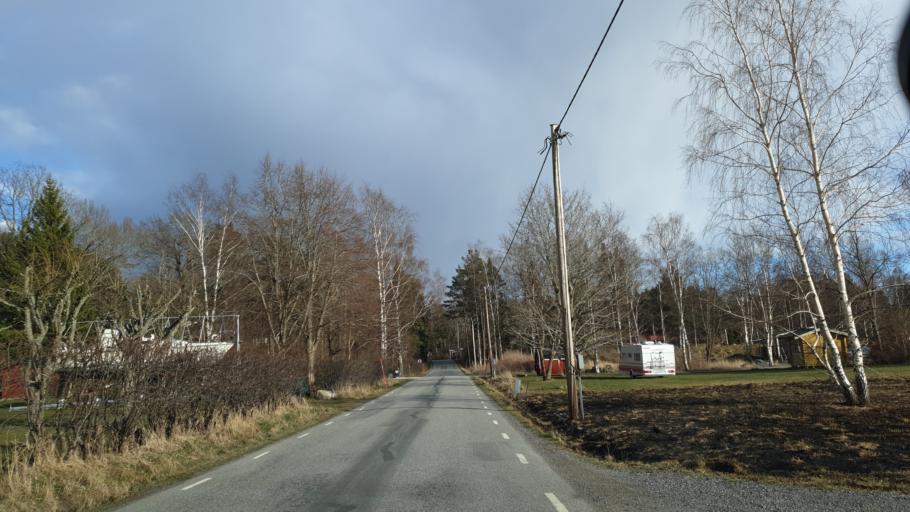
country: SE
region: Stockholm
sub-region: Varmdo Kommun
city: Holo
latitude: 59.3596
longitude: 18.6548
